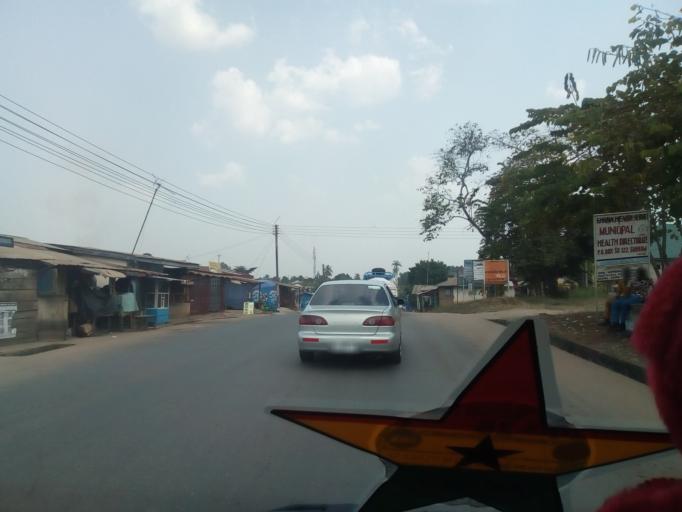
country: GH
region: Eastern
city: Suhum
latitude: 6.0413
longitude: -0.4437
